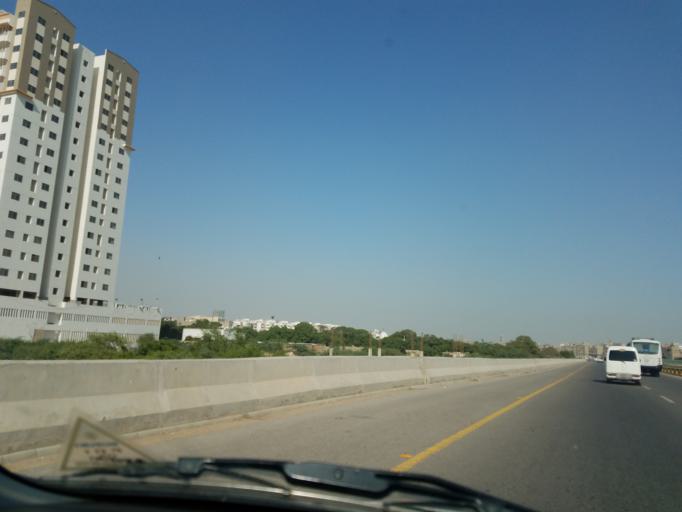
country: PK
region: Sindh
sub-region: Karachi District
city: Karachi
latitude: 24.9128
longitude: 67.0733
